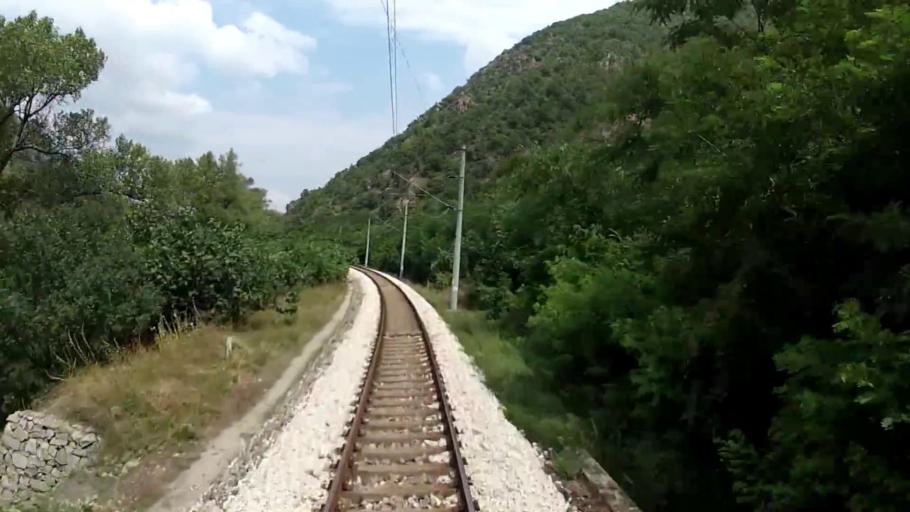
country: BG
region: Blagoevgrad
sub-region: Obshtina Kresna
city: Stara Kresna
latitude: 41.8329
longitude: 23.1557
